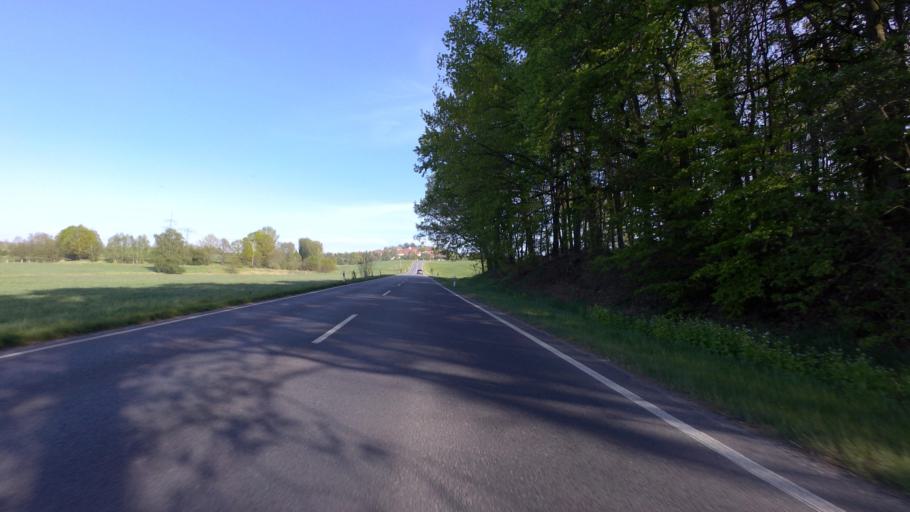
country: DE
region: Saxony
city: Stolpen
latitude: 51.0554
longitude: 14.0665
